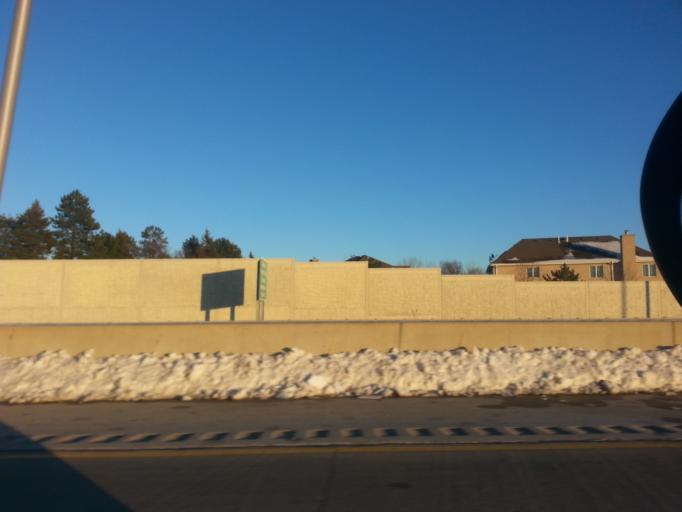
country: US
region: Illinois
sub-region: Cook County
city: Northbrook
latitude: 42.0949
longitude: -87.8682
